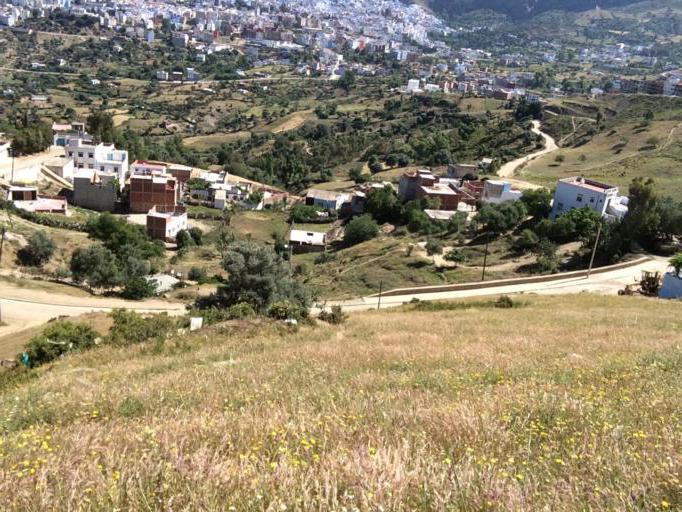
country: MA
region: Tanger-Tetouan
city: Chefchaouene
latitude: 35.1535
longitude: -5.2747
